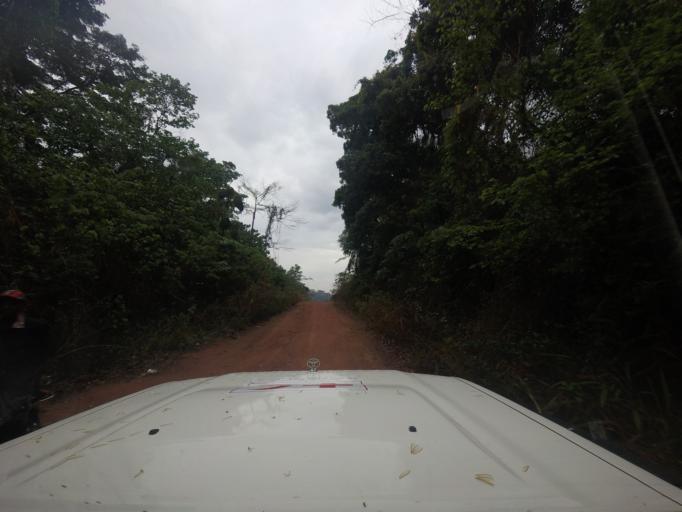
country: LR
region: Lofa
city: Voinjama
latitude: 8.3753
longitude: -9.8664
